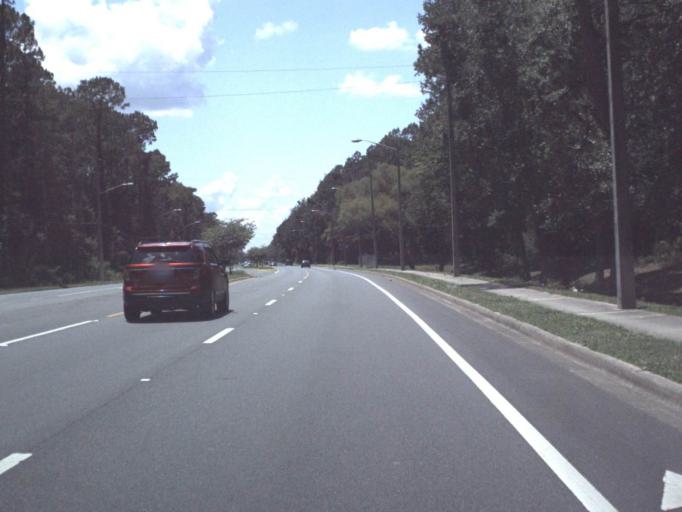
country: US
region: Florida
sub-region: Alachua County
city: Gainesville
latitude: 29.6883
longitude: -82.2986
